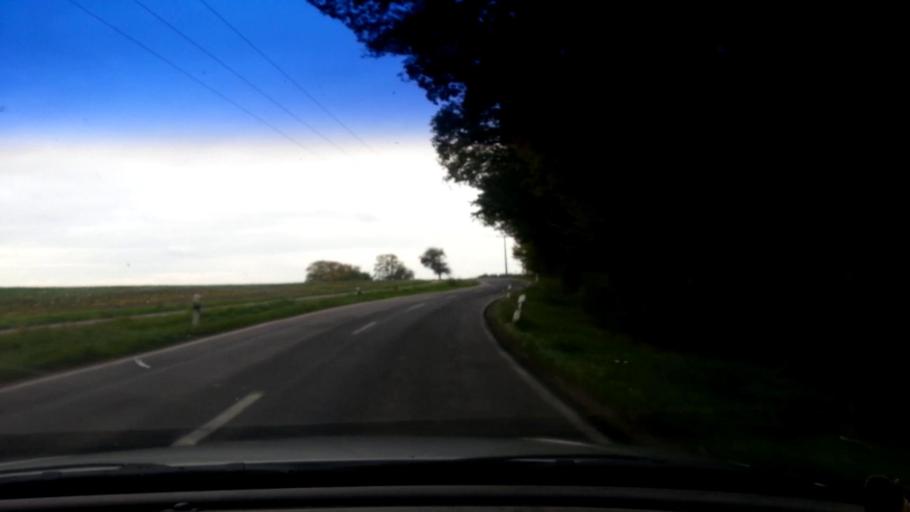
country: DE
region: Bavaria
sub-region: Upper Franconia
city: Priesendorf
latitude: 49.8959
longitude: 10.6547
